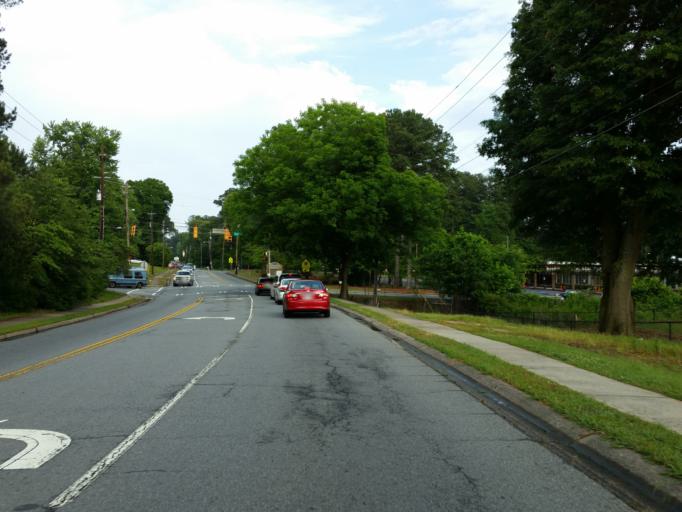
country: US
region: Georgia
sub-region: Cobb County
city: Smyrna
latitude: 33.9433
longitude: -84.4786
